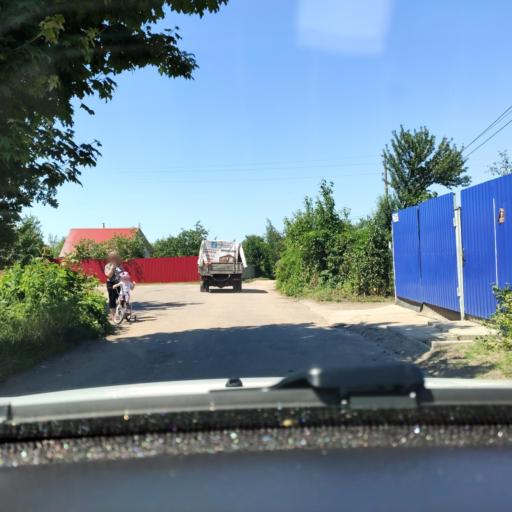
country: RU
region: Voronezj
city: Shilovo
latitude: 51.5926
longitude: 39.1459
